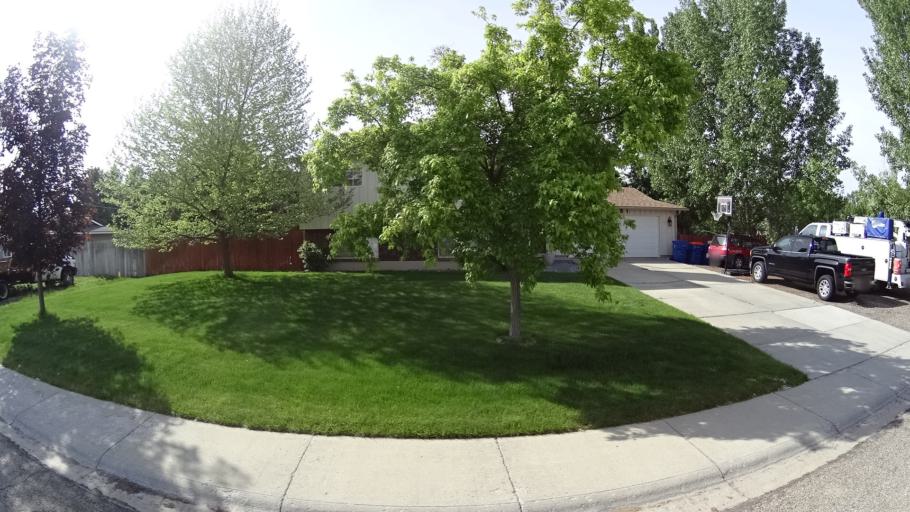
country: US
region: Idaho
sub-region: Ada County
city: Meridian
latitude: 43.5660
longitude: -116.3290
